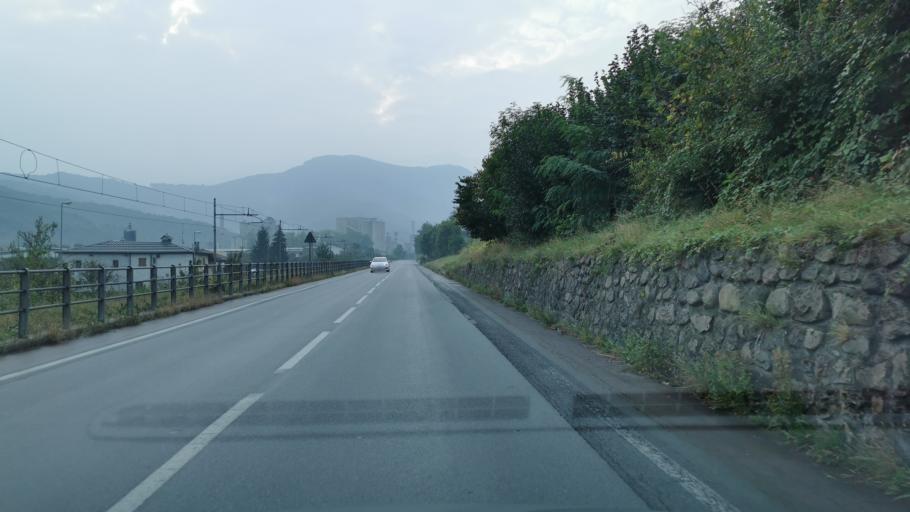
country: IT
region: Piedmont
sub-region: Provincia di Cuneo
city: Roccavione
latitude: 44.3068
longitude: 7.4963
